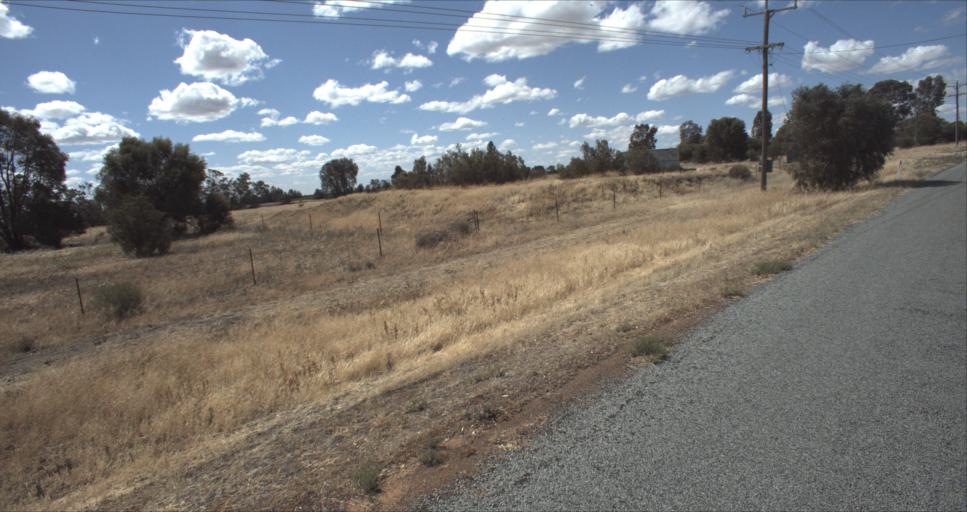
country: AU
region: New South Wales
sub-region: Leeton
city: Leeton
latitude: -34.5174
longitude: 146.2287
